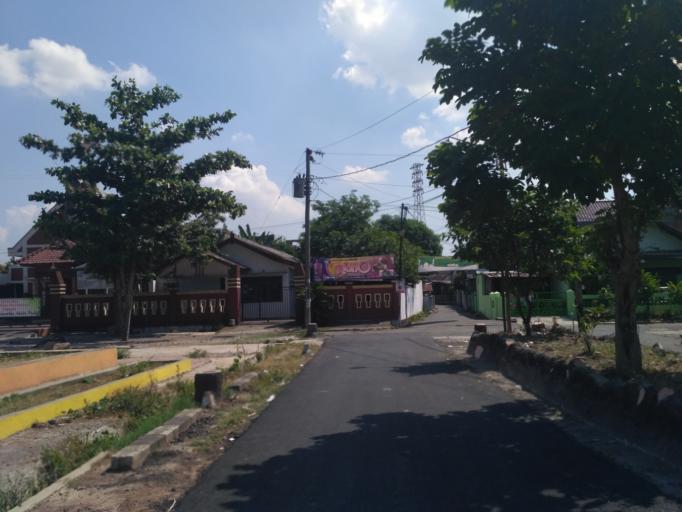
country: ID
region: Central Java
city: Semarang
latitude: -7.0047
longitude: 110.4422
